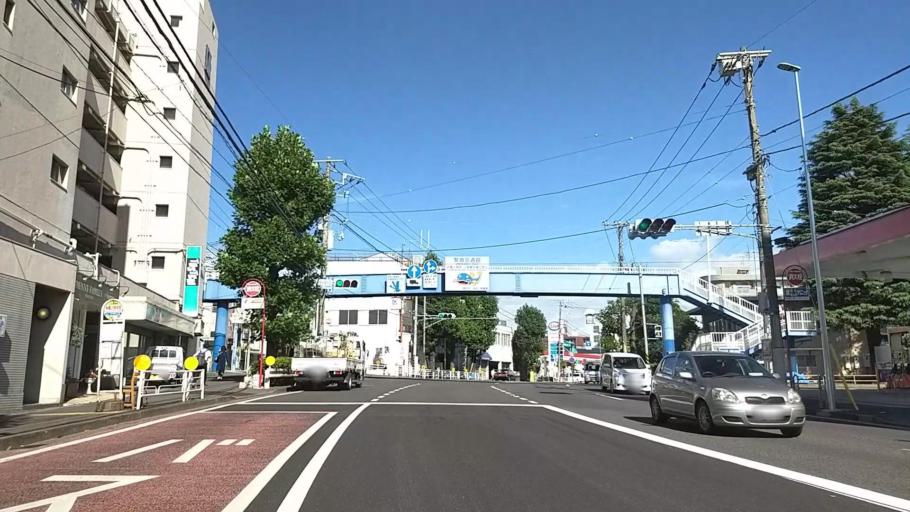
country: JP
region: Kanagawa
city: Yokohama
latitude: 35.4903
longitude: 139.6216
